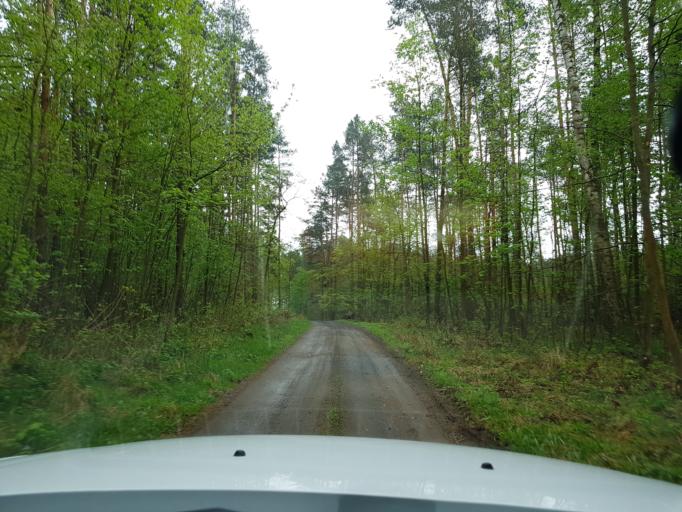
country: PL
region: West Pomeranian Voivodeship
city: Trzcinsko Zdroj
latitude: 52.9920
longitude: 14.6720
